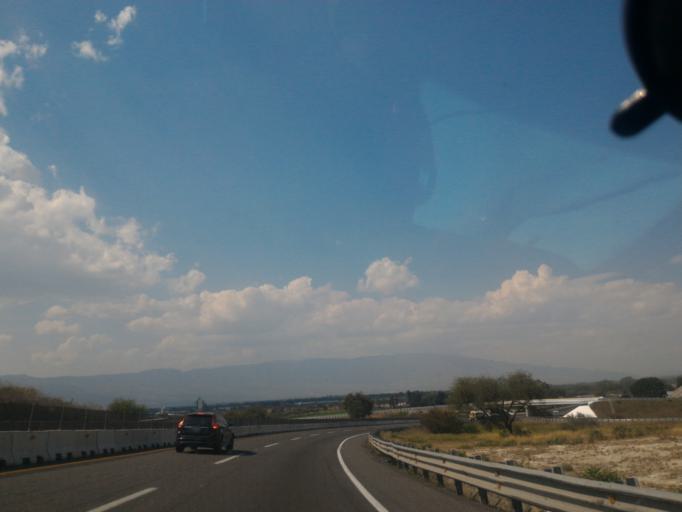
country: MX
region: Jalisco
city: Usmajac
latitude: 19.8766
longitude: -103.5164
